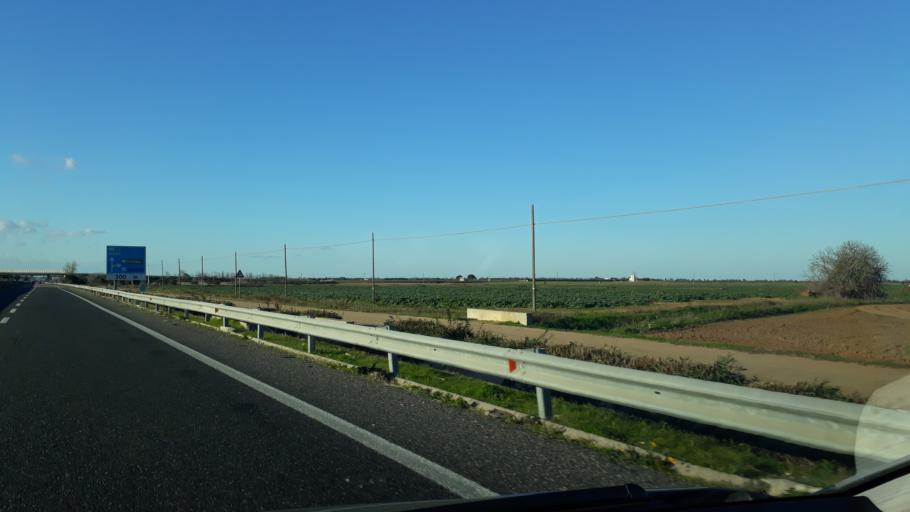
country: IT
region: Apulia
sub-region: Provincia di Brindisi
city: Brindisi
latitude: 40.6745
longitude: 17.8501
